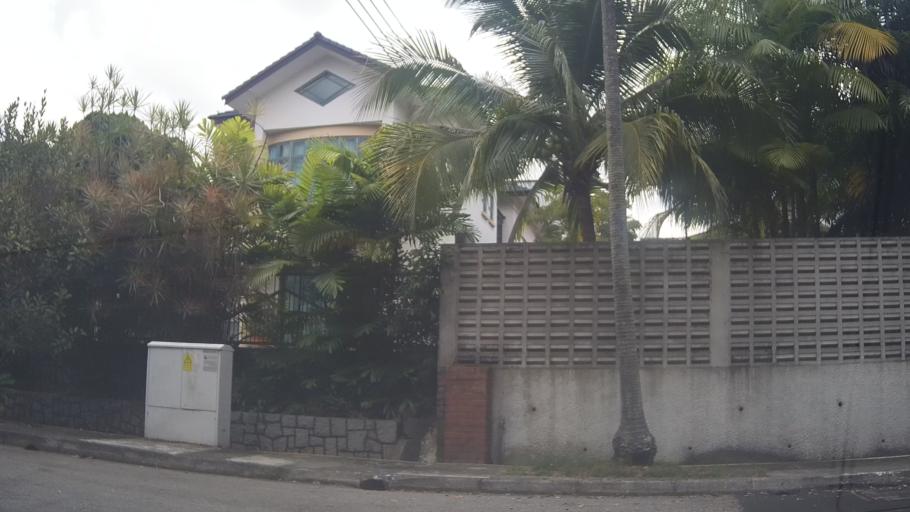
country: SG
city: Singapore
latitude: 1.3626
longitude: 103.8700
